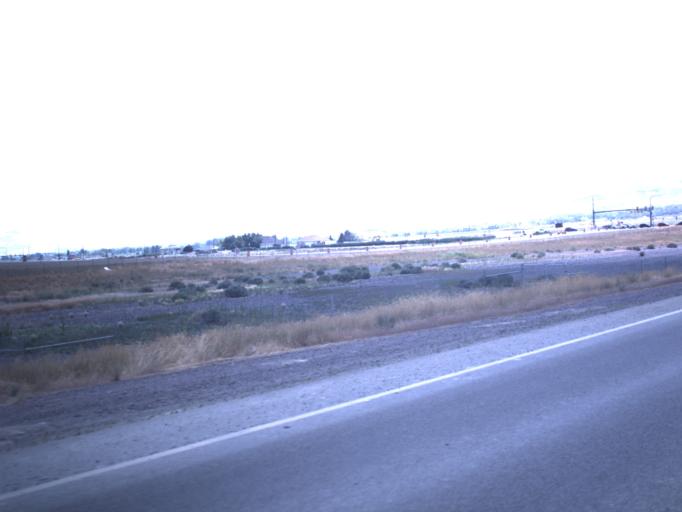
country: US
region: Utah
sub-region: Salt Lake County
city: Herriman
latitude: 40.5109
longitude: -112.0051
